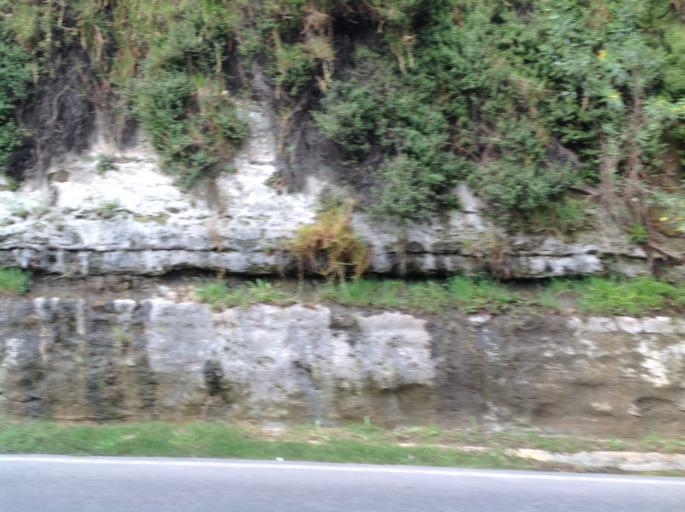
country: MX
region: Mexico
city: Ciudad Lopez Mateos
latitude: 19.6047
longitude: -99.2263
